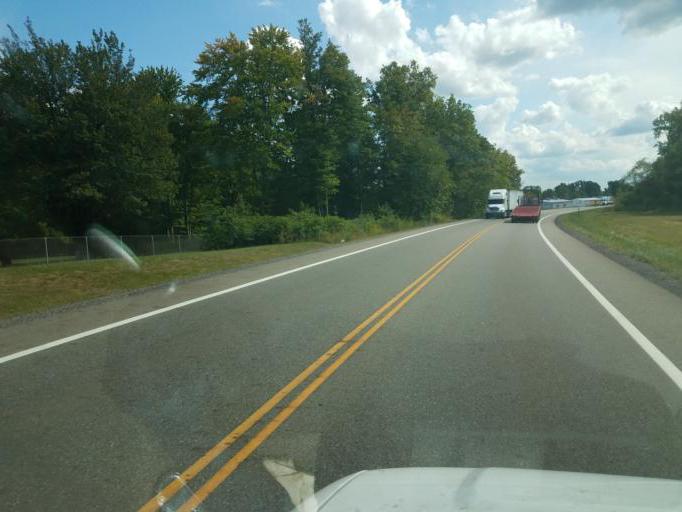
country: US
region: Ohio
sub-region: Portage County
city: Ravenna
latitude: 41.1665
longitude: -81.2200
